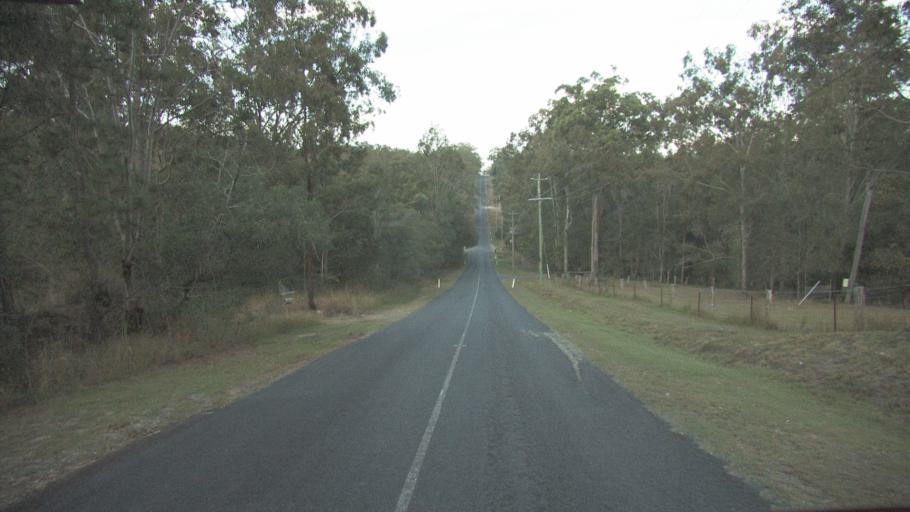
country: AU
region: Queensland
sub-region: Logan
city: Cedar Vale
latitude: -27.8372
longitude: 153.0870
